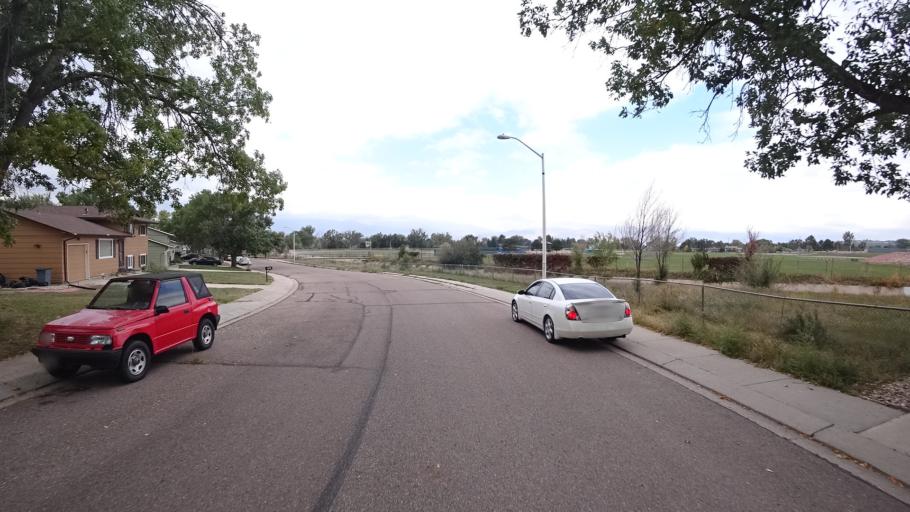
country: US
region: Colorado
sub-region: El Paso County
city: Cimarron Hills
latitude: 38.8925
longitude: -104.7424
